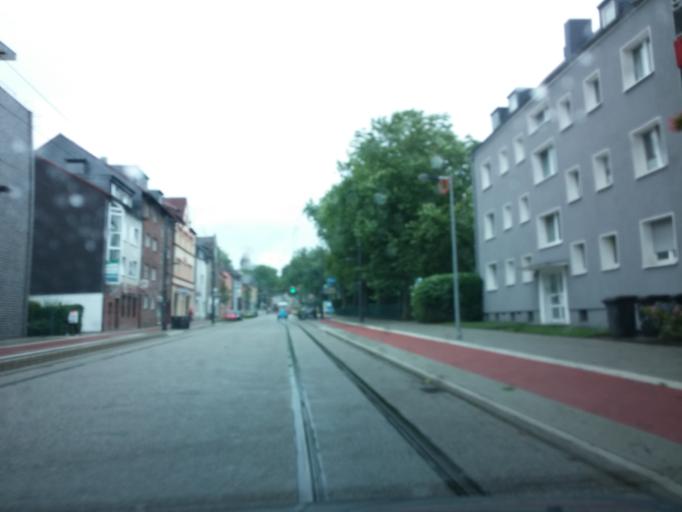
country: DE
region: North Rhine-Westphalia
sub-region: Regierungsbezirk Munster
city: Gladbeck
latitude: 51.5666
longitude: 7.0465
